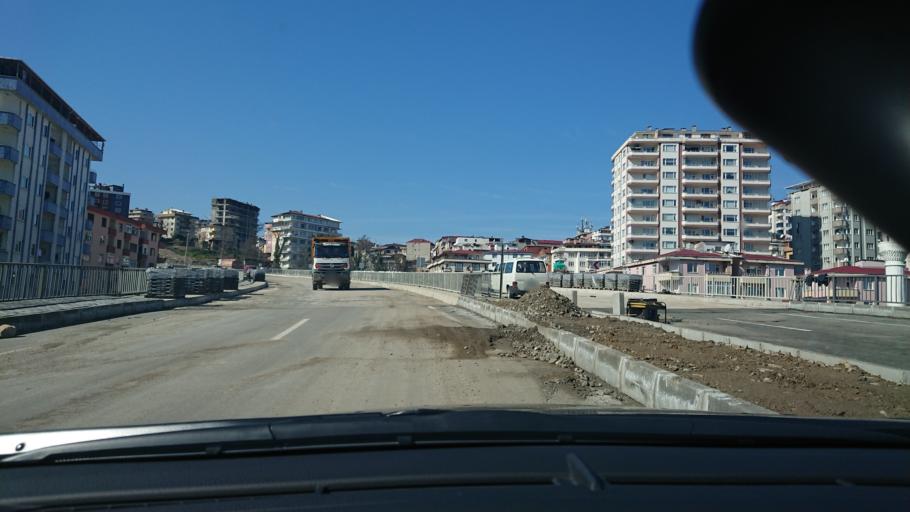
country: TR
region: Rize
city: Rize
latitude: 41.0215
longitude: 40.5268
